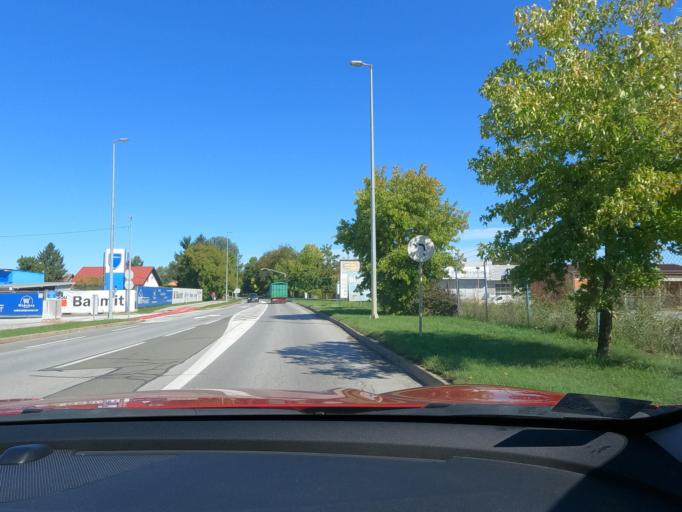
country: HR
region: Sisacko-Moslavacka
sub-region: Grad Sisak
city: Sisak
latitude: 45.4917
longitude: 16.3816
